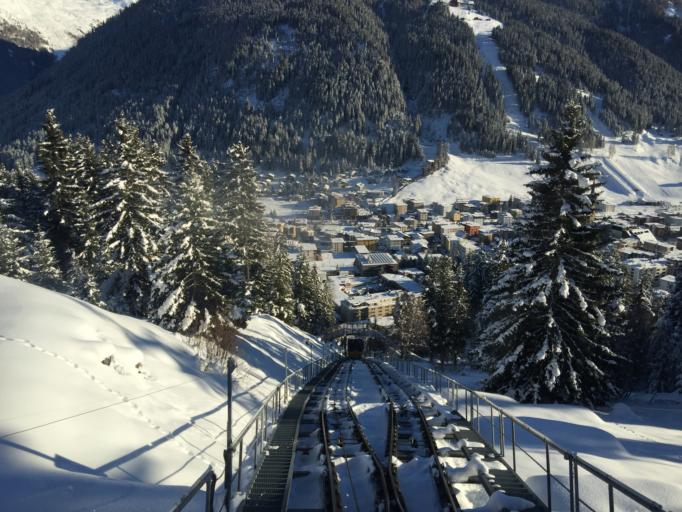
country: CH
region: Grisons
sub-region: Praettigau/Davos District
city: Davos
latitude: 46.7993
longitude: 9.8180
